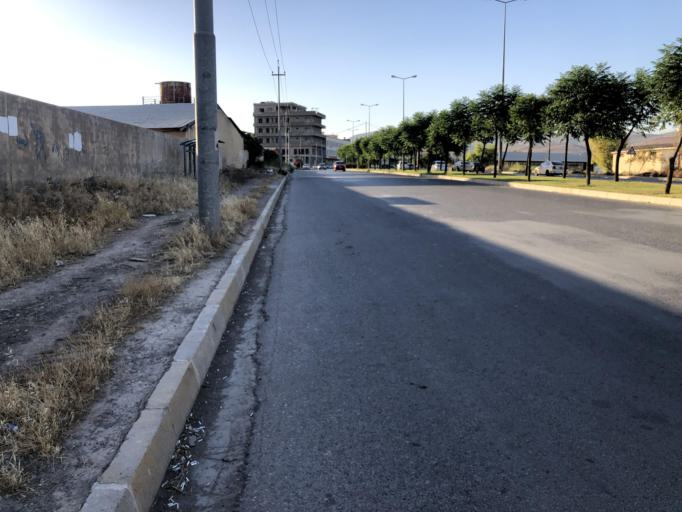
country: IQ
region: Dahuk
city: Dihok
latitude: 36.8574
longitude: 42.9344
